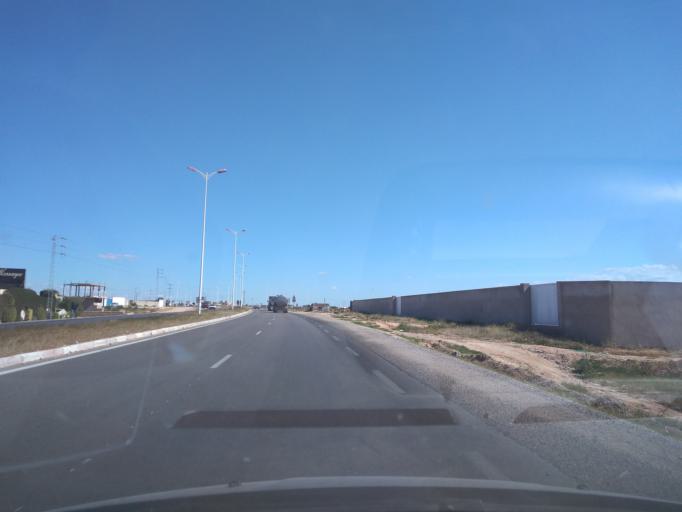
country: TN
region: Safaqis
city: Sfax
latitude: 34.8007
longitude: 10.6867
